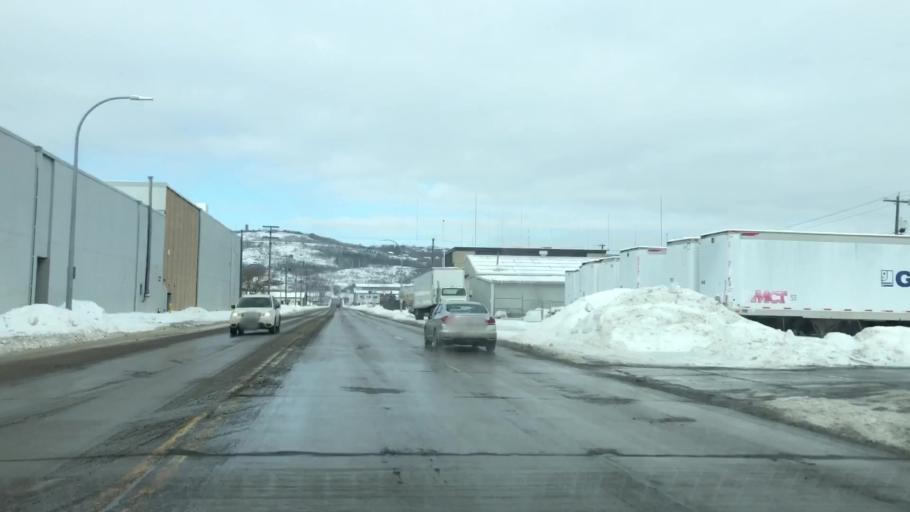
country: US
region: Minnesota
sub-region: Saint Louis County
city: Duluth
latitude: 46.7604
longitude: -92.1097
